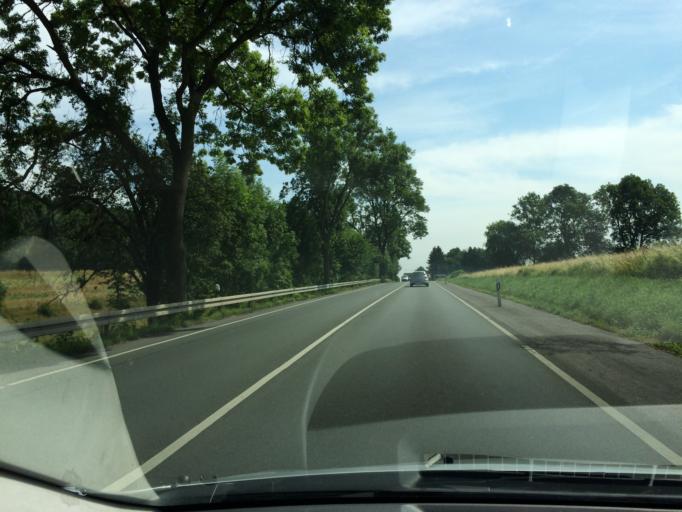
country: DE
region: North Rhine-Westphalia
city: Hemer
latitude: 51.3861
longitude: 7.7360
